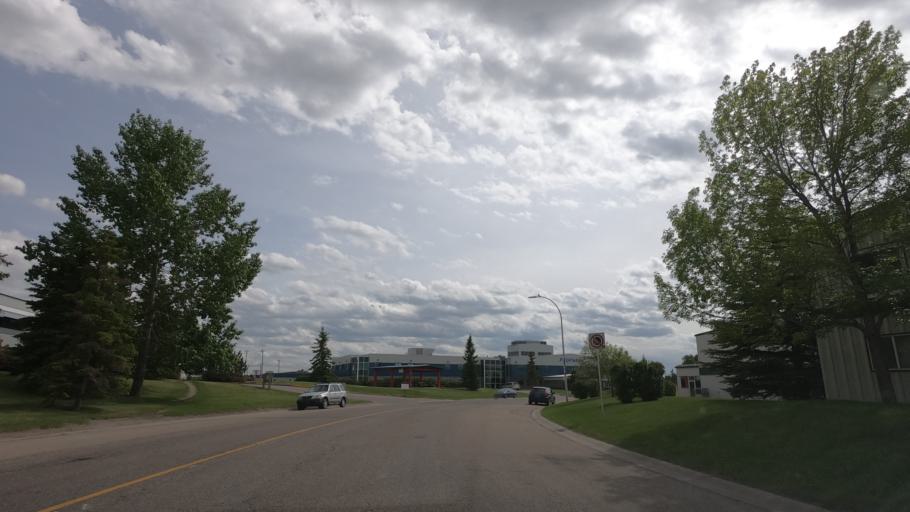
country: CA
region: Alberta
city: Airdrie
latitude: 51.2895
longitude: -113.9808
